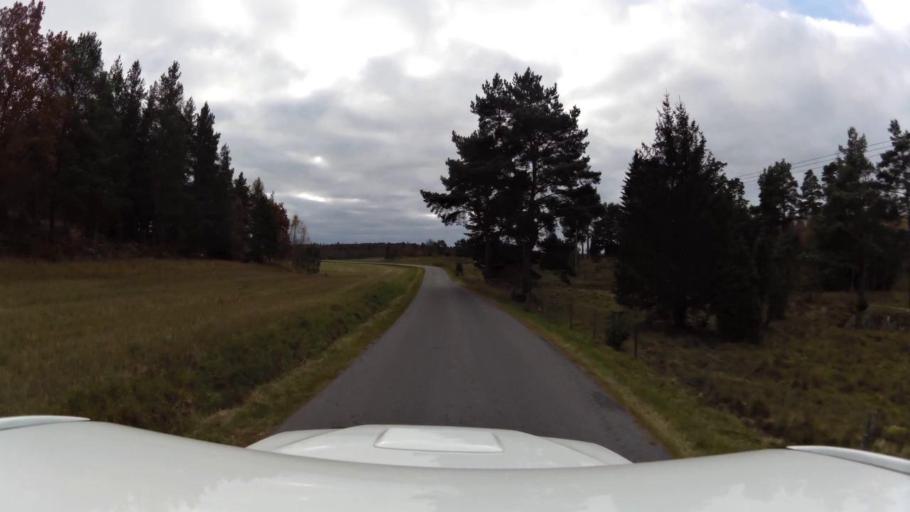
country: SE
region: OEstergoetland
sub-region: Linkopings Kommun
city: Linghem
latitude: 58.3905
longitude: 15.8357
